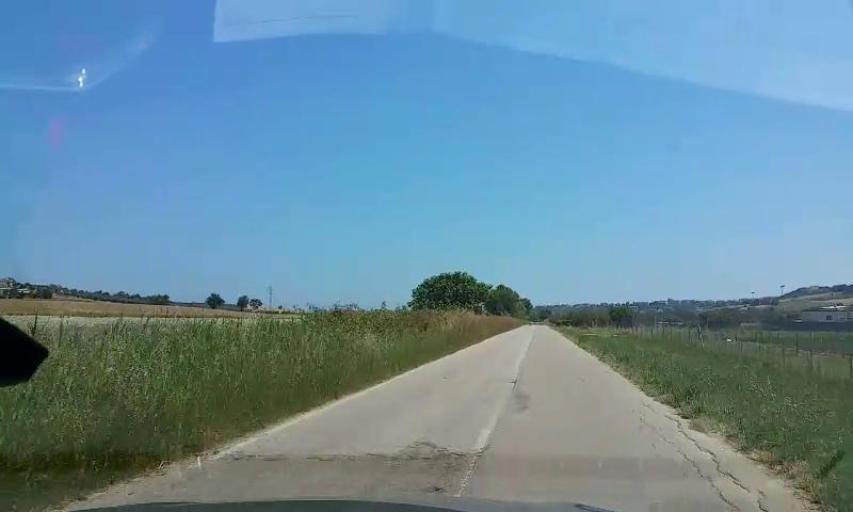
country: IT
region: Molise
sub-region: Provincia di Campobasso
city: San Giacomo degli Schiavoni
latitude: 41.9881
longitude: 14.9405
